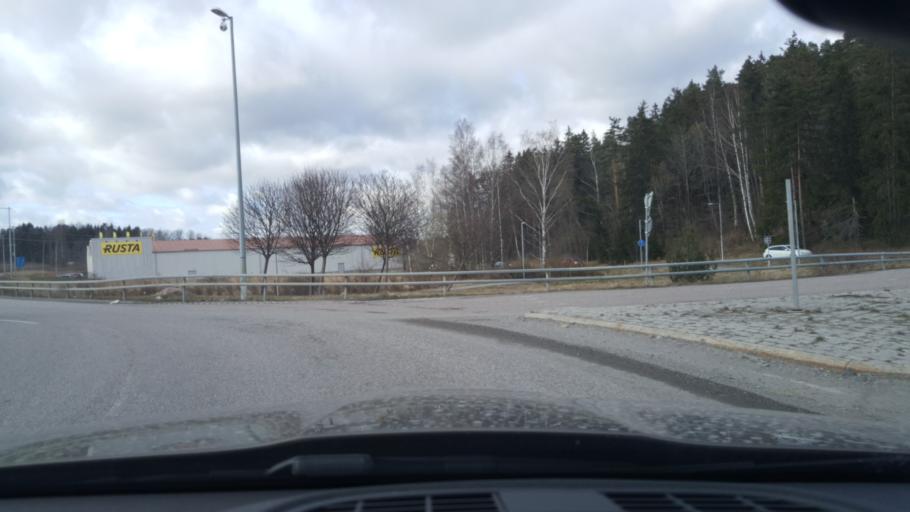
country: SE
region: Stockholm
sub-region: Osterakers Kommun
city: Akersberga
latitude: 59.4870
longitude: 18.2777
